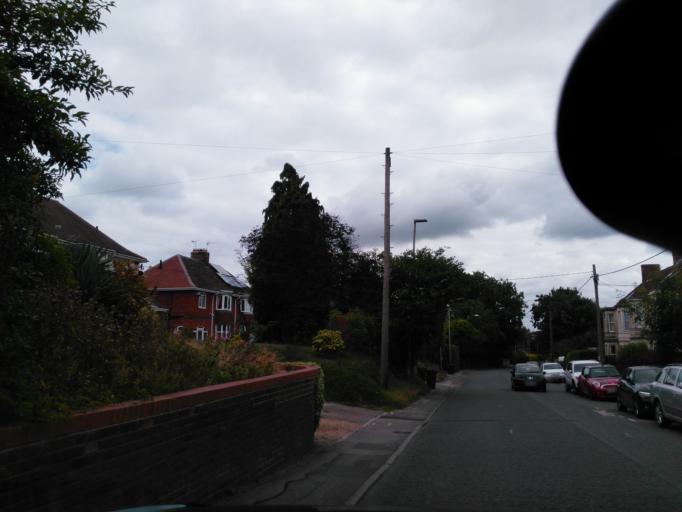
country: GB
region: England
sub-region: Wiltshire
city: Trowbridge
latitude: 51.3244
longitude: -2.2249
